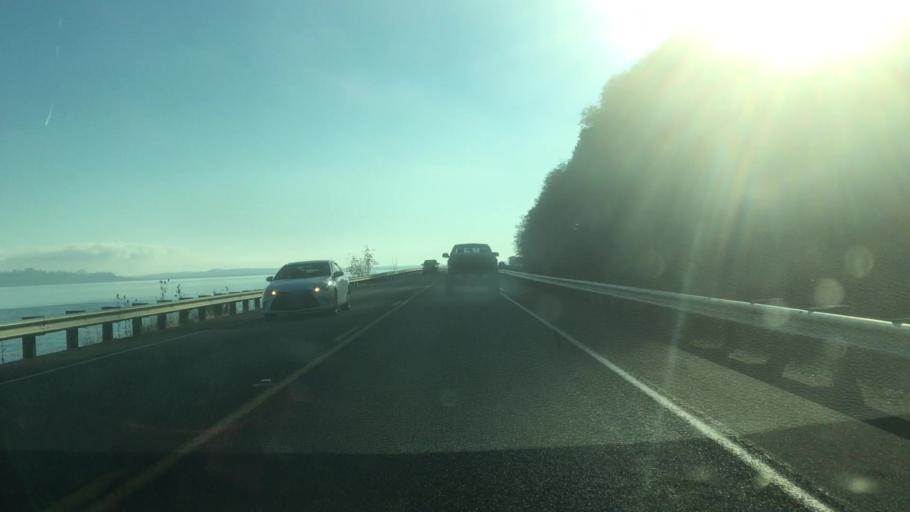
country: US
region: Oregon
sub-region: Clatsop County
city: Astoria
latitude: 46.2648
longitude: -123.8377
